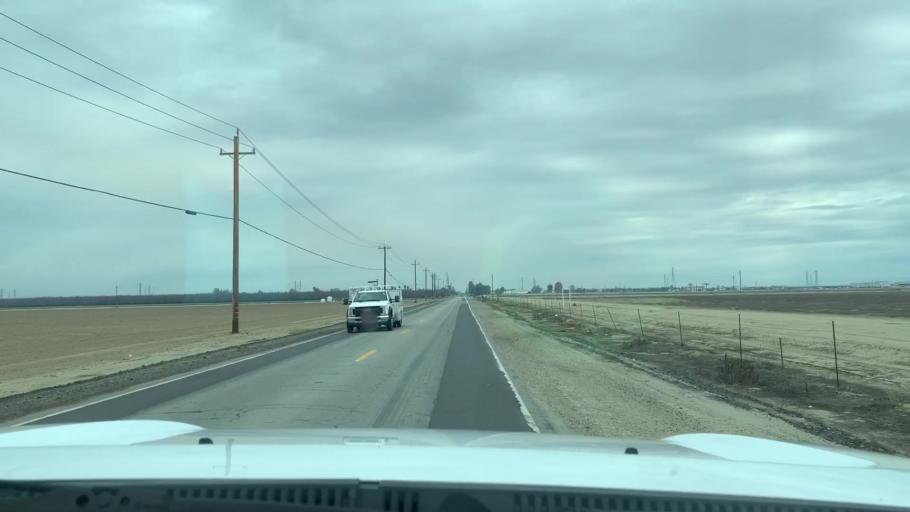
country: US
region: California
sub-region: Kern County
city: Rosedale
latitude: 35.3729
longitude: -119.2521
